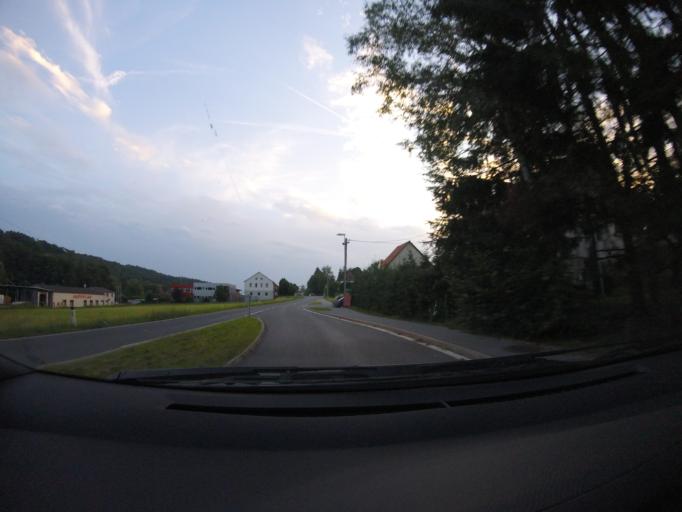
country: AT
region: Styria
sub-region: Politischer Bezirk Graz-Umgebung
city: Hart bei Graz
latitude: 47.0618
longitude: 15.5532
